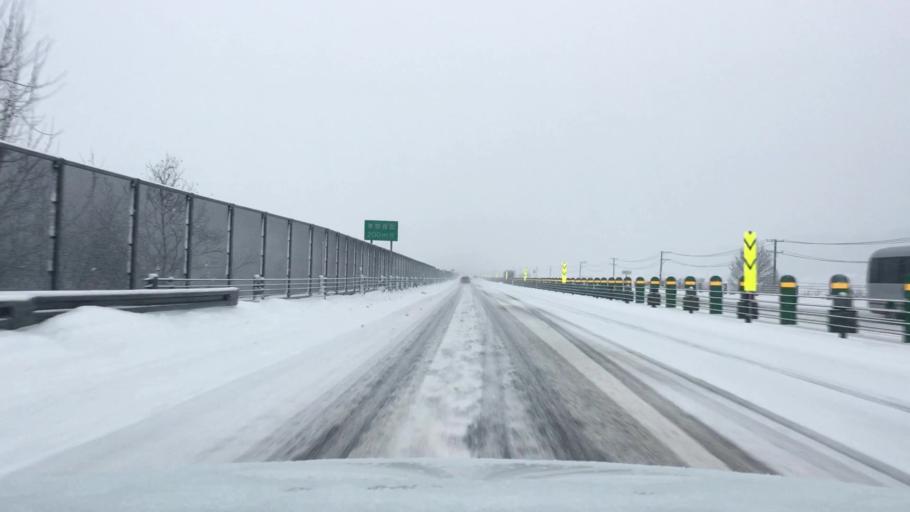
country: JP
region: Akita
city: Hanawa
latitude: 40.2808
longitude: 140.7608
